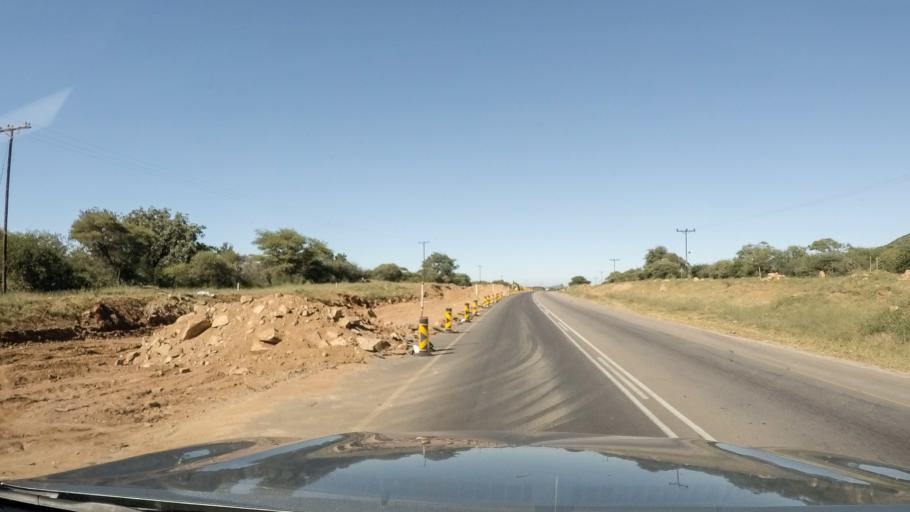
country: BW
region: South East
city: Gaborone
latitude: -24.7086
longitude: 25.8668
